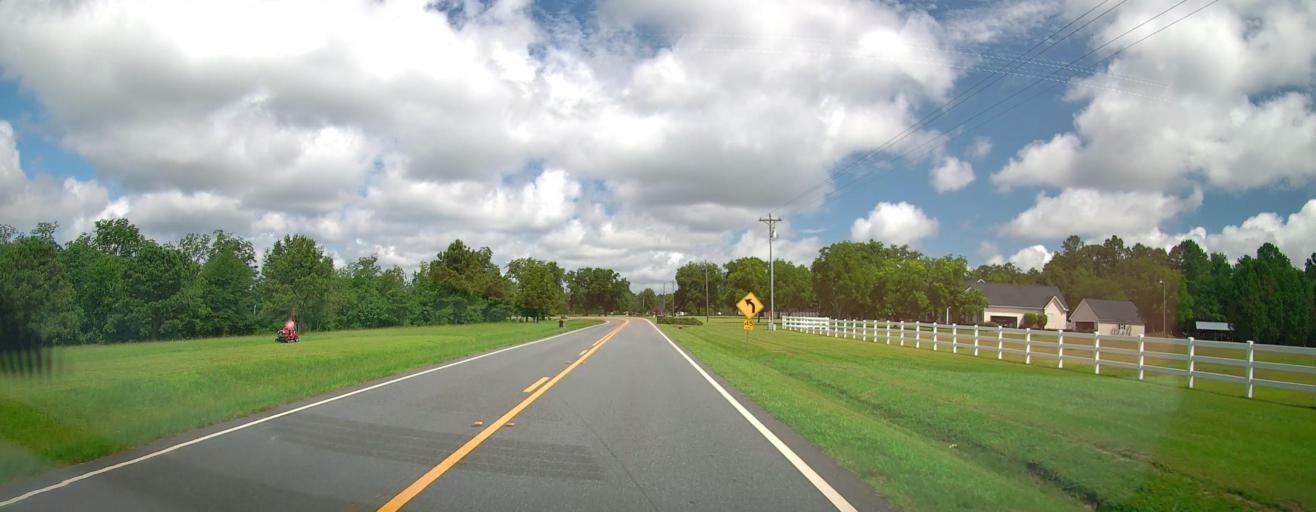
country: US
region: Georgia
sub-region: Peach County
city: Byron
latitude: 32.6791
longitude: -83.8408
